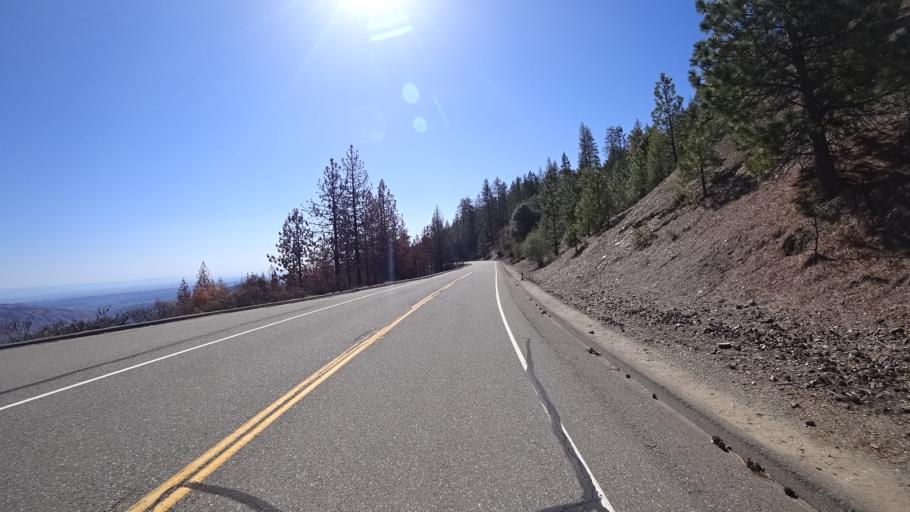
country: US
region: California
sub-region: Tehama County
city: Rancho Tehama Reserve
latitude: 39.6803
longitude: -122.7077
